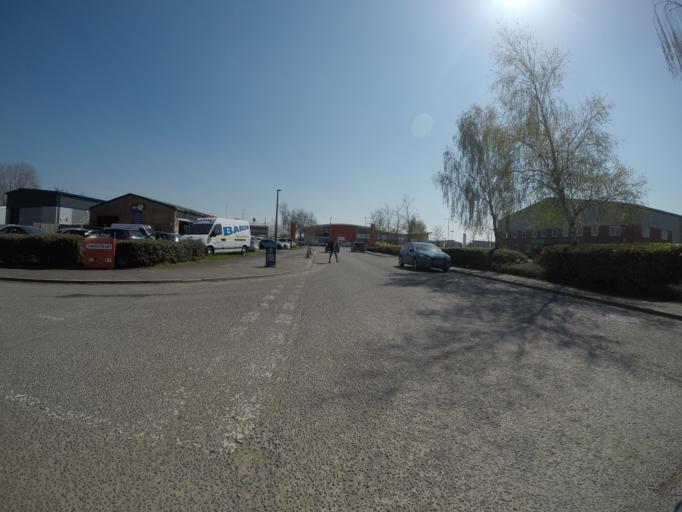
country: GB
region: England
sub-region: City of York
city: Wigginton
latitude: 53.9882
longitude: -1.0935
